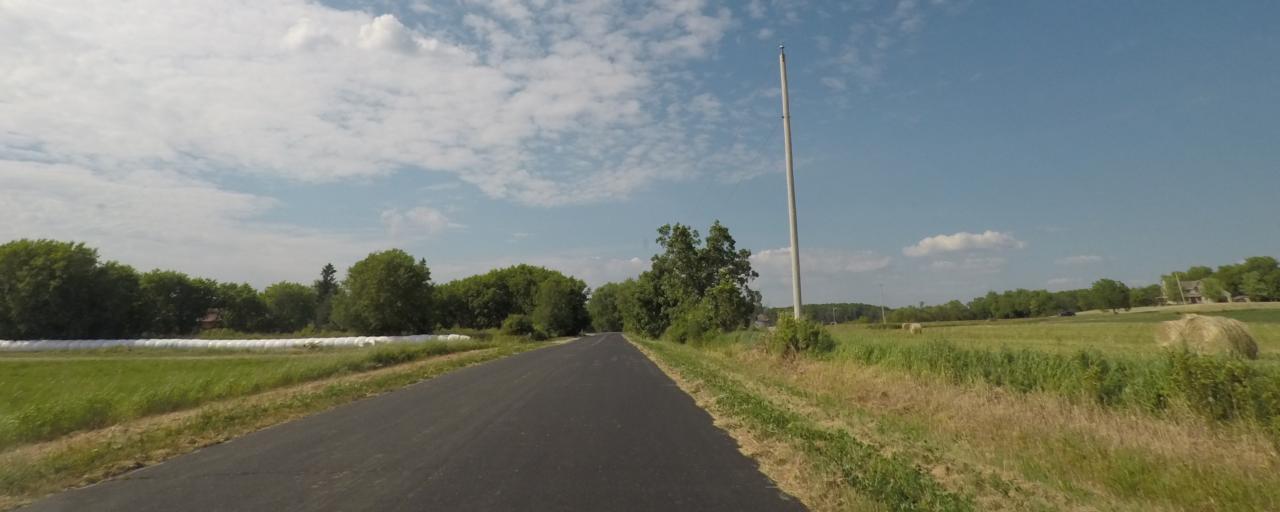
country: US
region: Wisconsin
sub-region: Waukesha County
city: Eagle
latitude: 42.7916
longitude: -88.5289
